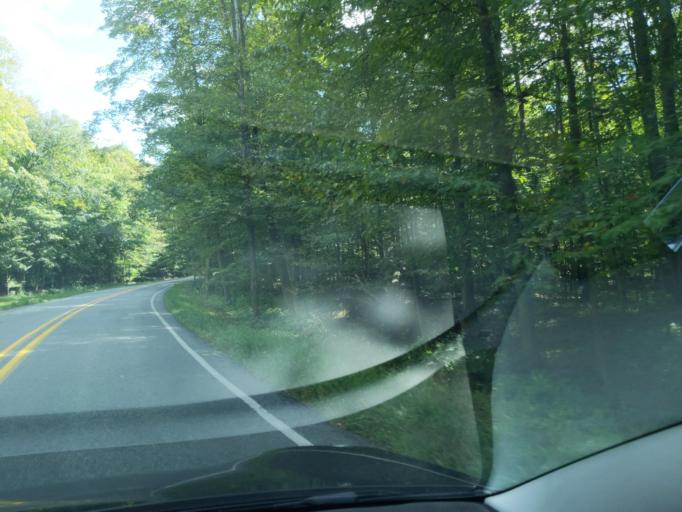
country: US
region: Michigan
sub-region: Antrim County
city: Bellaire
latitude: 45.0239
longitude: -85.2936
